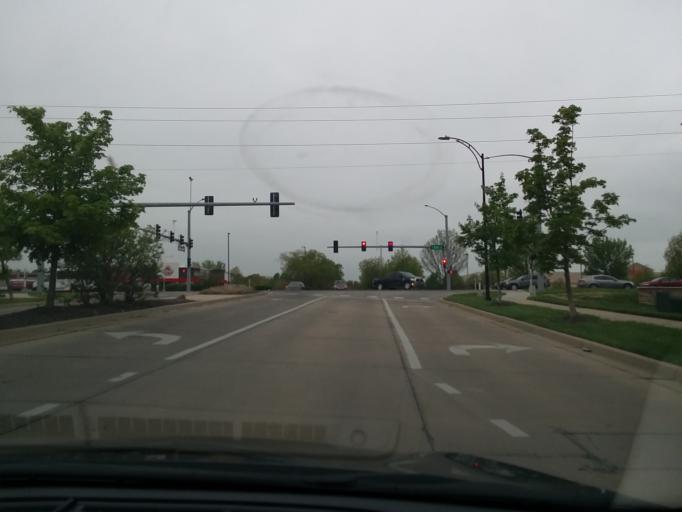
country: US
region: Kansas
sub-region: Douglas County
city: Lawrence
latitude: 38.9720
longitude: -95.3030
